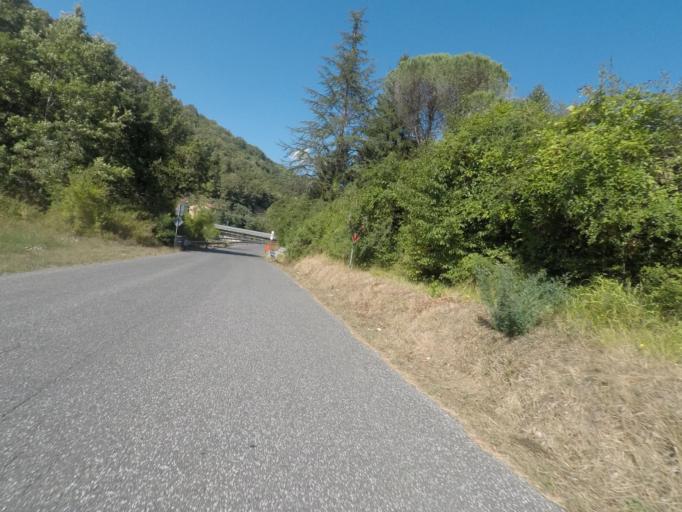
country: IT
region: Tuscany
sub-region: Provincia di Massa-Carrara
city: Pallerone
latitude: 44.2012
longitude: 10.0616
